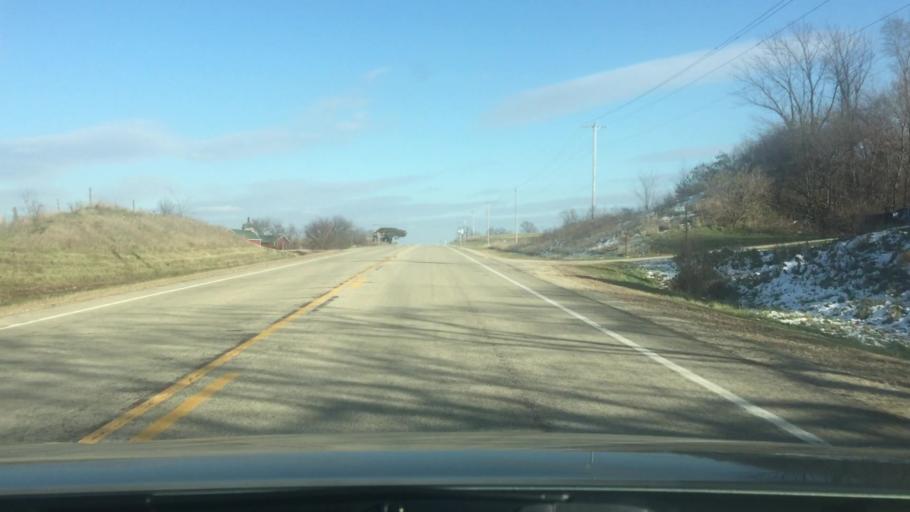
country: US
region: Wisconsin
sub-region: Jefferson County
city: Palmyra
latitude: 42.9328
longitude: -88.6489
